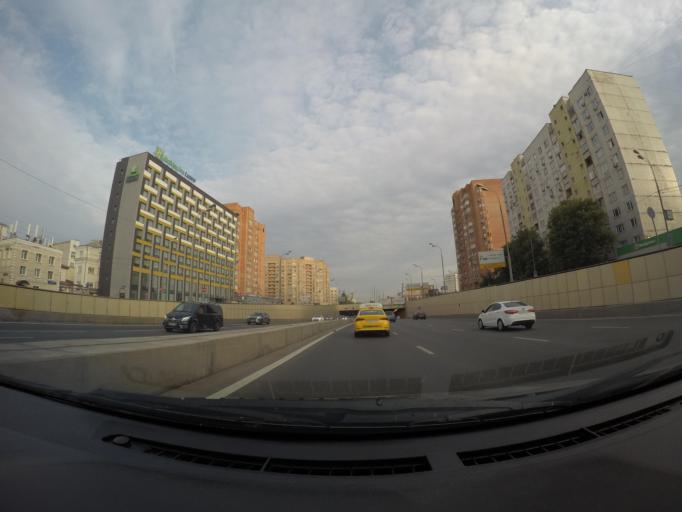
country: RU
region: Moscow
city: Lefortovo
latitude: 55.7764
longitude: 37.6818
